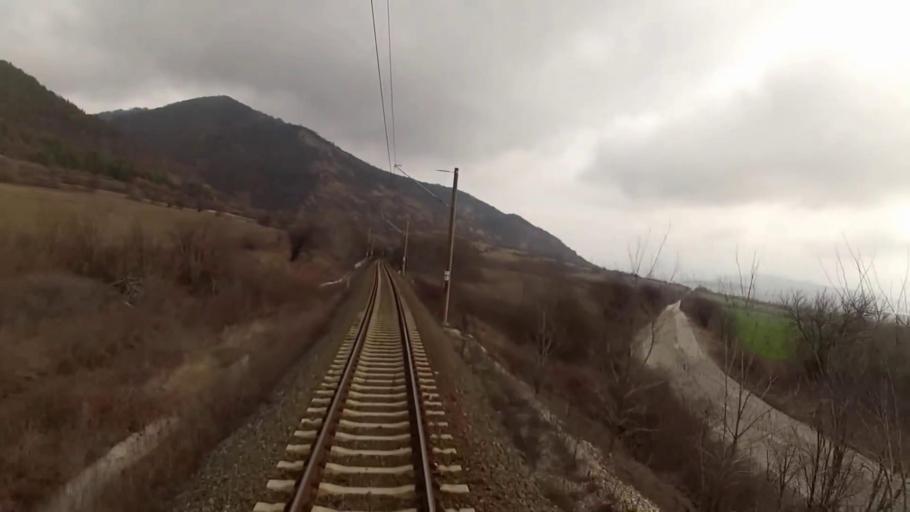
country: BG
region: Sofiya
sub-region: Obshtina Chelopech
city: Chelopech
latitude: 42.6930
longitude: 24.0455
